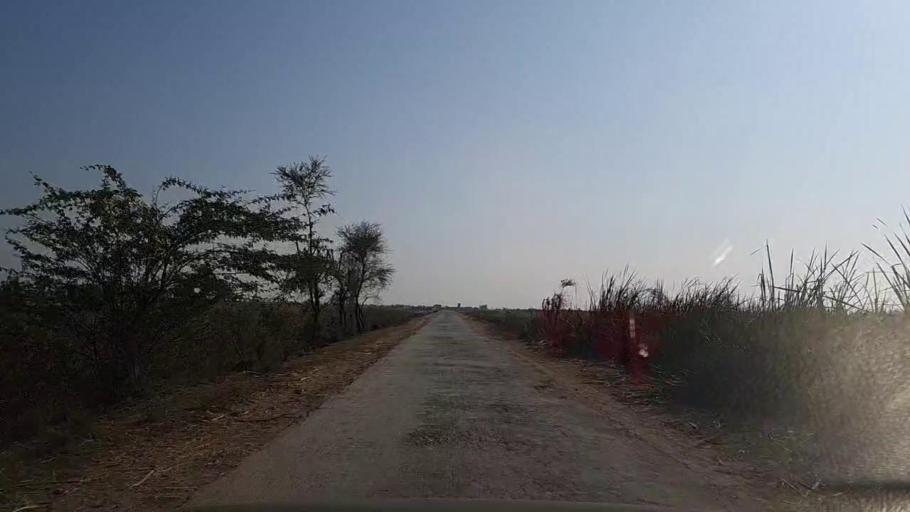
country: PK
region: Sindh
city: Sanghar
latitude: 26.0045
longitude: 69.0226
